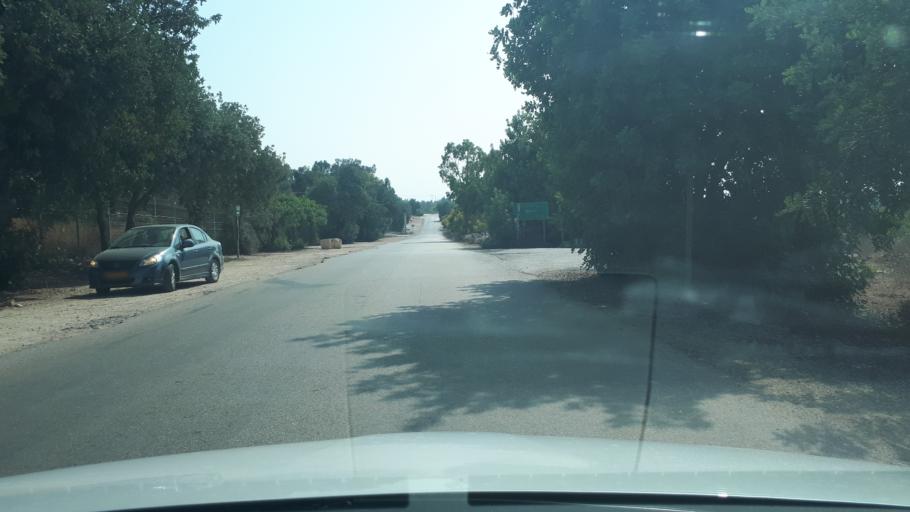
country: IL
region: Central District
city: Rosh Ha'Ayin
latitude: 32.0654
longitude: 34.9468
